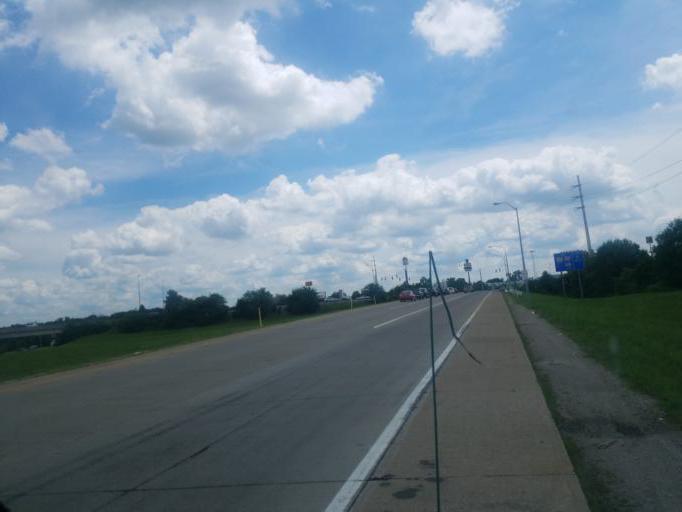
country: US
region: Kentucky
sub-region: Bullitt County
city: Brooks
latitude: 38.0645
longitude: -85.7004
